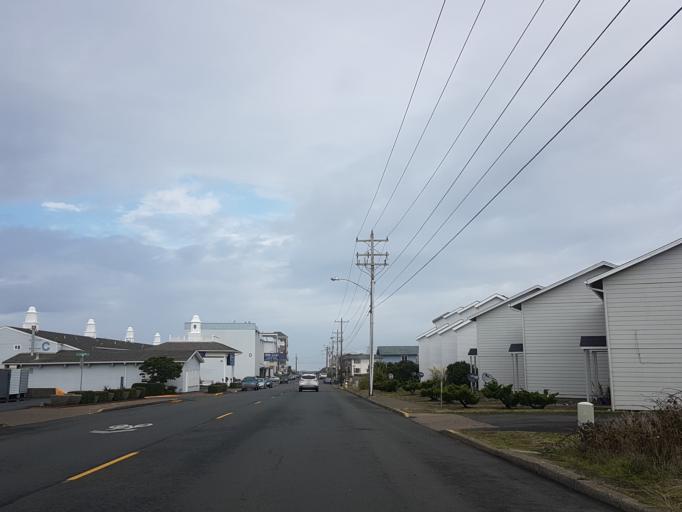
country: US
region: Oregon
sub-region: Lincoln County
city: Newport
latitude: 44.6314
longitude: -124.0633
